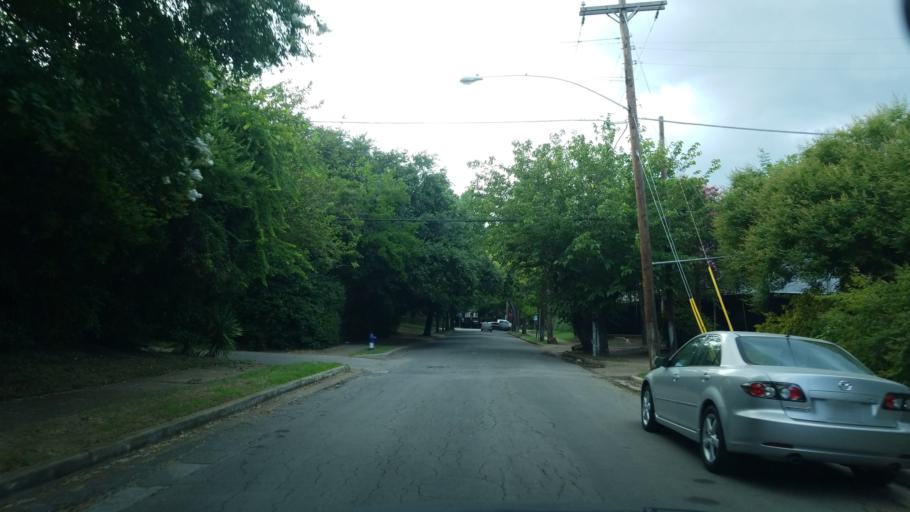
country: US
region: Texas
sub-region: Dallas County
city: Highland Park
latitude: 32.8062
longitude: -96.7667
